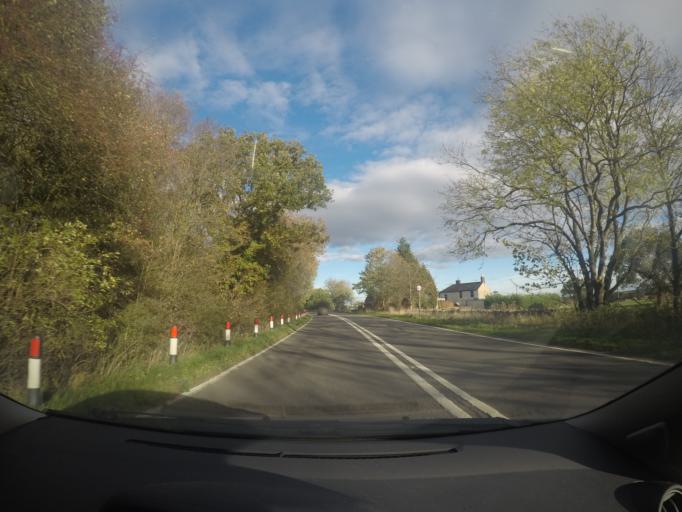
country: GB
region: England
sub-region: City and Borough of Leeds
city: Thorner
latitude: 53.8445
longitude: -1.4140
